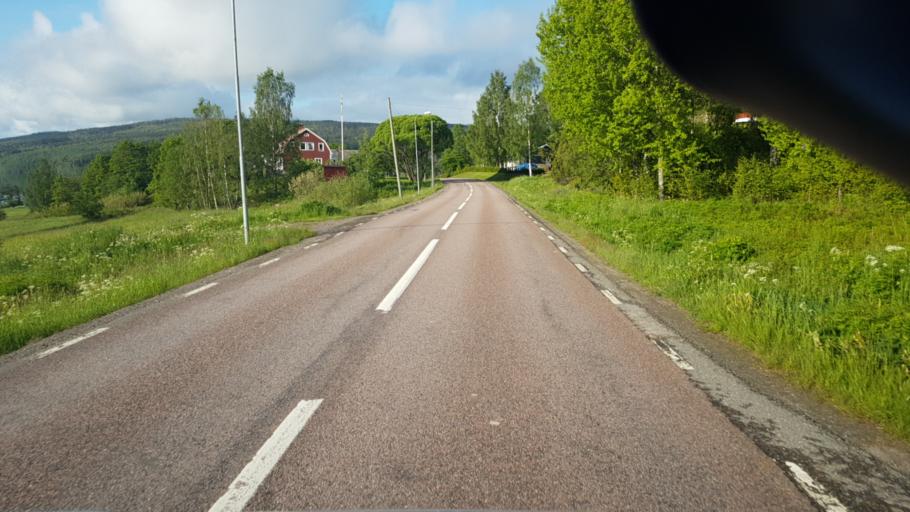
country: SE
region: Vaermland
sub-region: Eda Kommun
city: Amotfors
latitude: 59.7717
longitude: 12.2732
